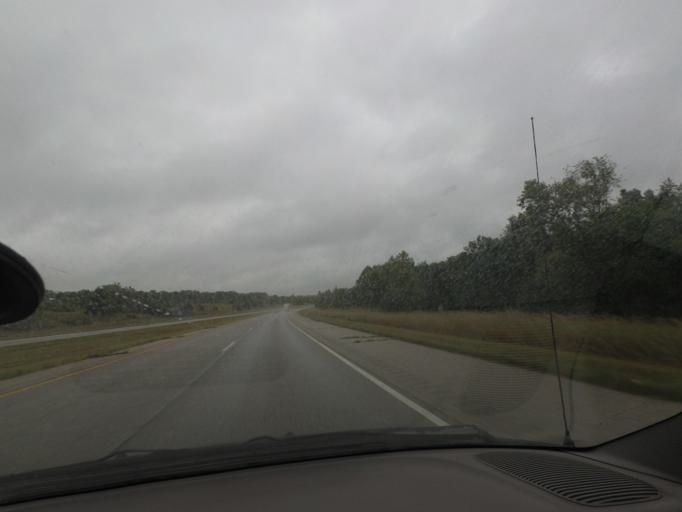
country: US
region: Illinois
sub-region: Pike County
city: Barry
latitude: 39.7238
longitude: -91.1148
